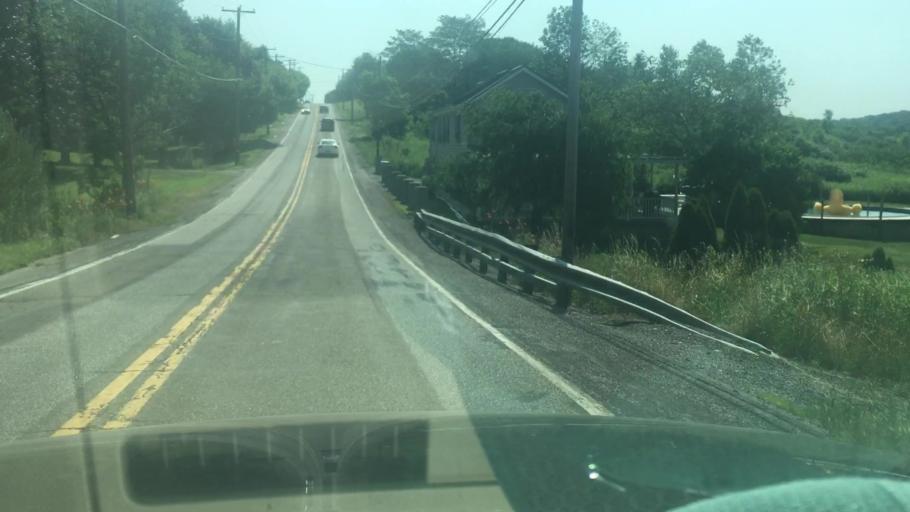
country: US
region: Pennsylvania
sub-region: Schuylkill County
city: Mahanoy City
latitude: 40.8186
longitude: -76.0705
